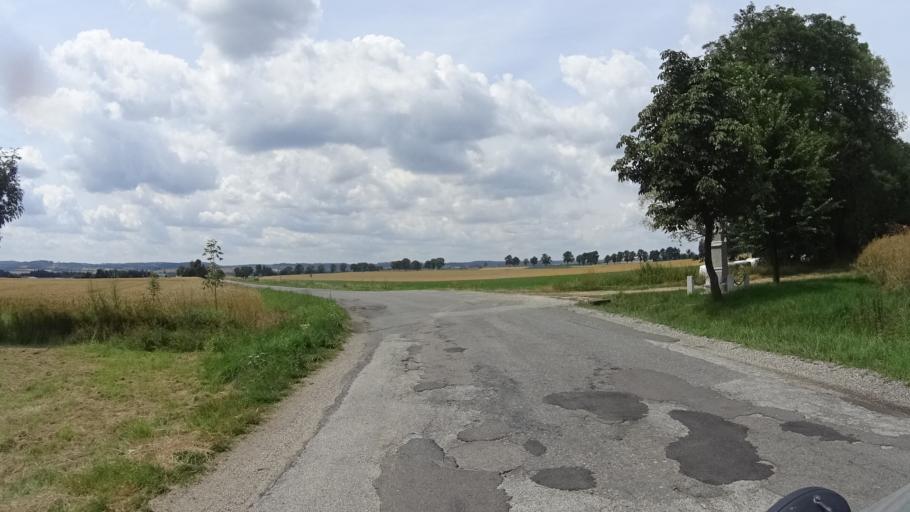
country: CZ
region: Vysocina
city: Merin
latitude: 49.4068
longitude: 15.9246
